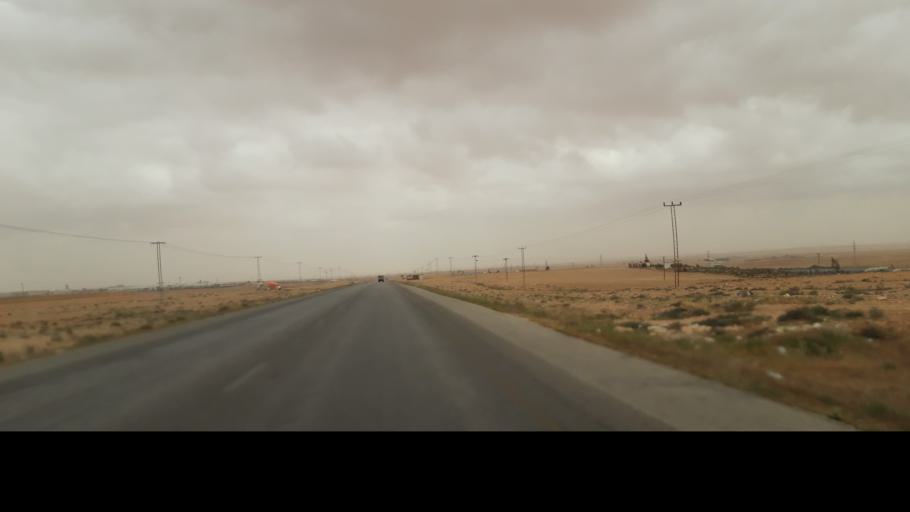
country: JO
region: Amman
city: Sahab
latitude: 31.7982
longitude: 36.1825
